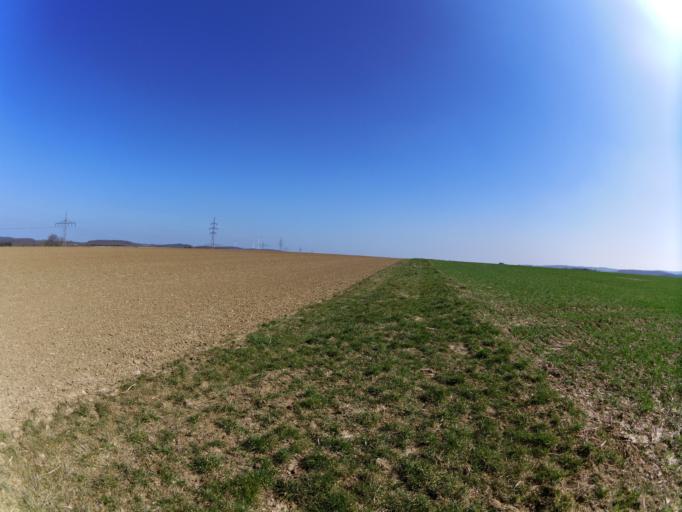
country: DE
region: Bavaria
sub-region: Regierungsbezirk Unterfranken
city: Greussenheim
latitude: 49.8065
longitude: 9.7759
